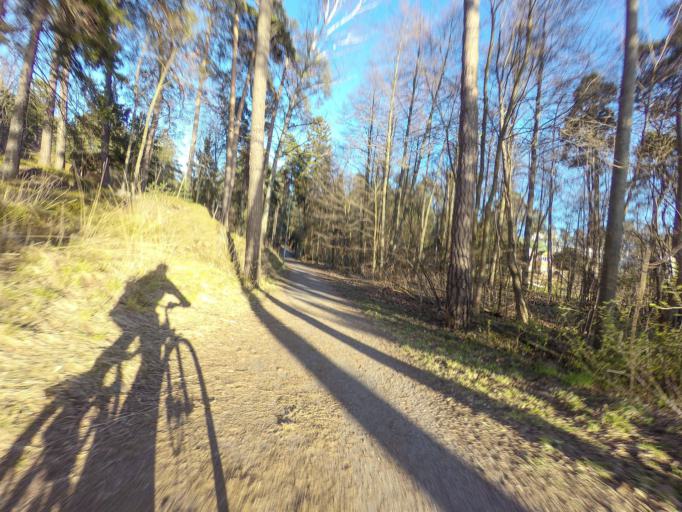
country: FI
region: Uusimaa
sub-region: Helsinki
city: Helsinki
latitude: 60.1774
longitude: 25.0217
